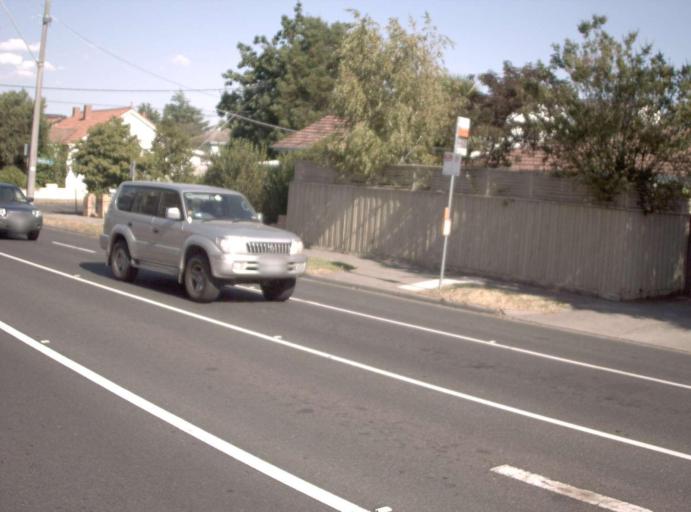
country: AU
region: Victoria
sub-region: Glen Eira
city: Glen Huntly
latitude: -37.8872
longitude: 145.0463
